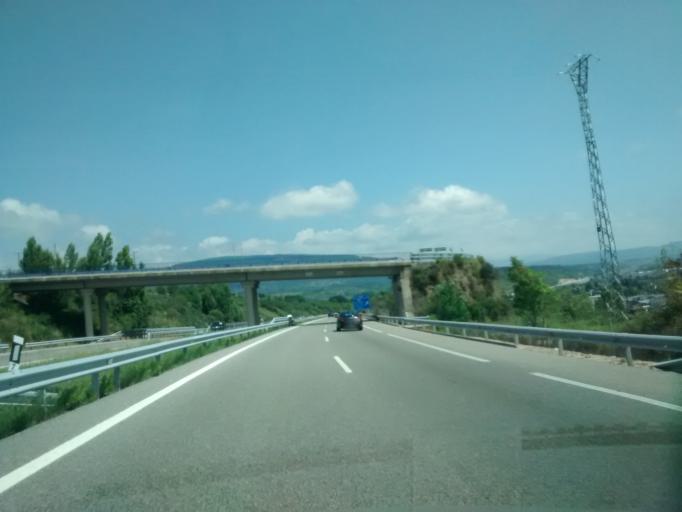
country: ES
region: Castille and Leon
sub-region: Provincia de Leon
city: Congosto
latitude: 42.5841
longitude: -6.5281
